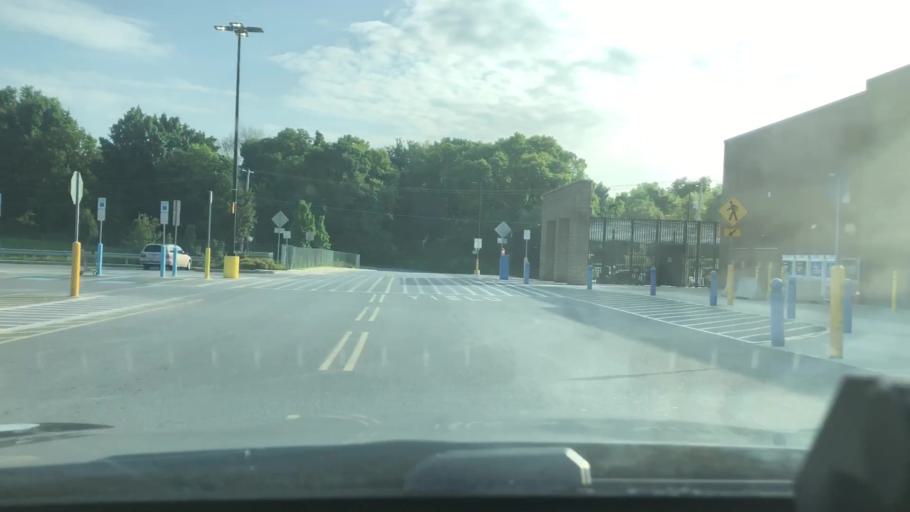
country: US
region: Pennsylvania
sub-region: Lehigh County
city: Catasauqua
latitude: 40.6458
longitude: -75.4877
